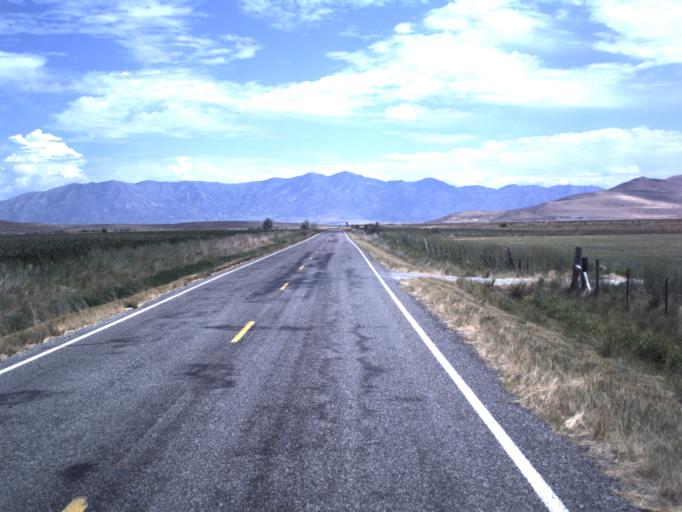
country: US
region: Utah
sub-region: Box Elder County
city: Tremonton
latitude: 41.6369
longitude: -112.3226
